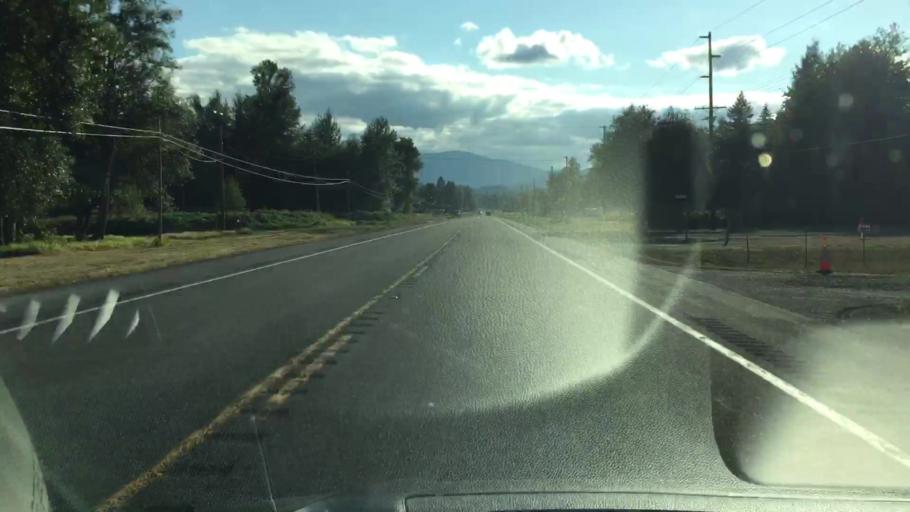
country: US
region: Washington
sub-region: Lewis County
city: Morton
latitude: 46.5337
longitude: -122.1229
